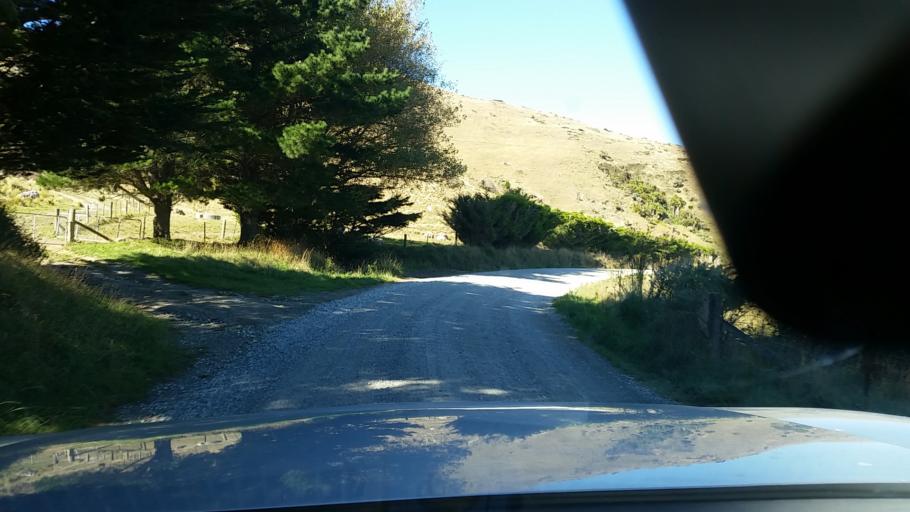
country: NZ
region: Marlborough
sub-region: Marlborough District
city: Blenheim
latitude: -41.8386
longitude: 174.1807
